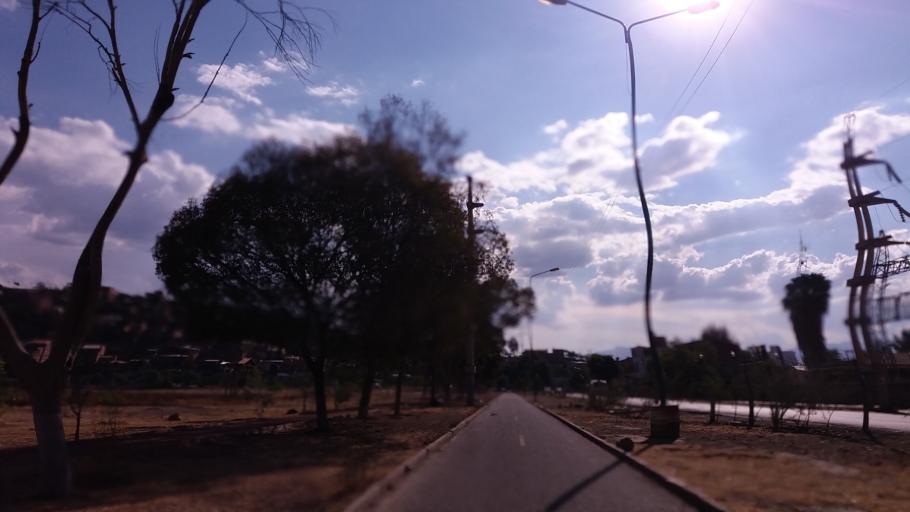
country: BO
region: Cochabamba
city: Cochabamba
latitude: -17.4009
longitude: -66.1434
